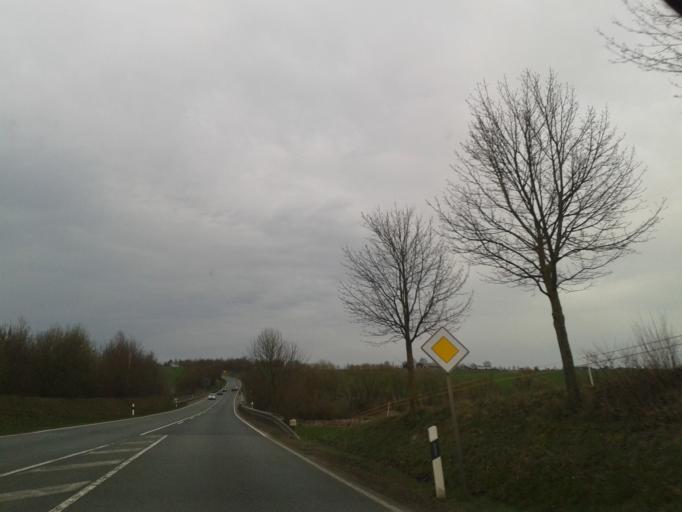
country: DE
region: Hesse
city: Frankenberg
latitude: 51.0516
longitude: 8.8158
